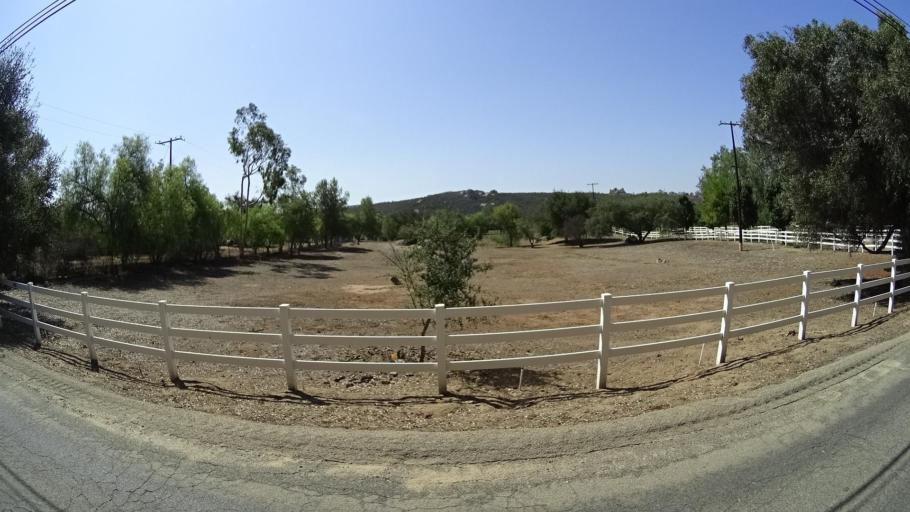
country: US
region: California
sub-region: San Diego County
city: Valley Center
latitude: 33.2709
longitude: -117.0383
